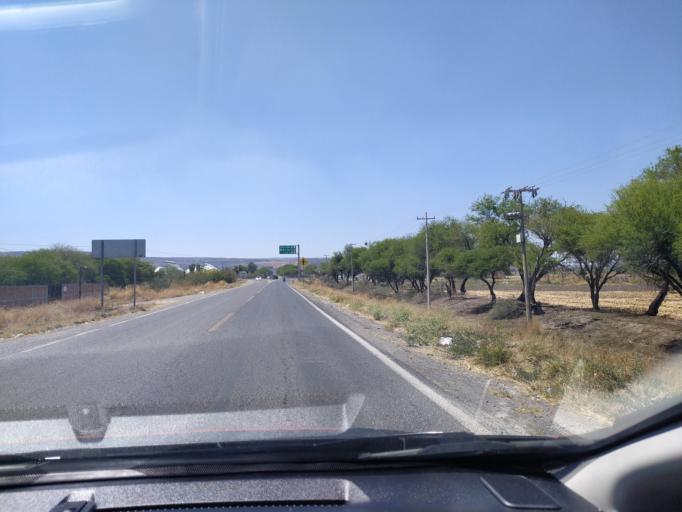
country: MX
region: Guanajuato
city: Ciudad Manuel Doblado
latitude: 20.7411
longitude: -101.9287
